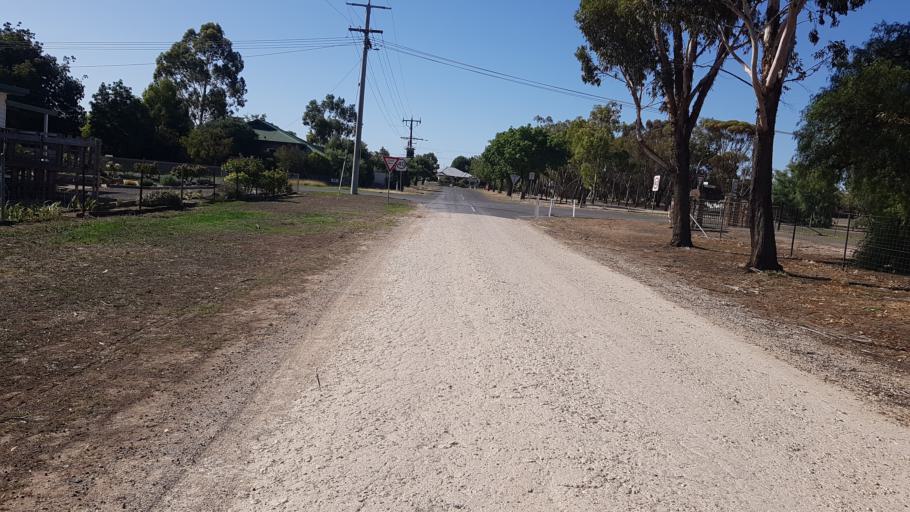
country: AU
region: Victoria
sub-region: Horsham
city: Horsham
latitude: -36.7423
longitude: 141.9473
